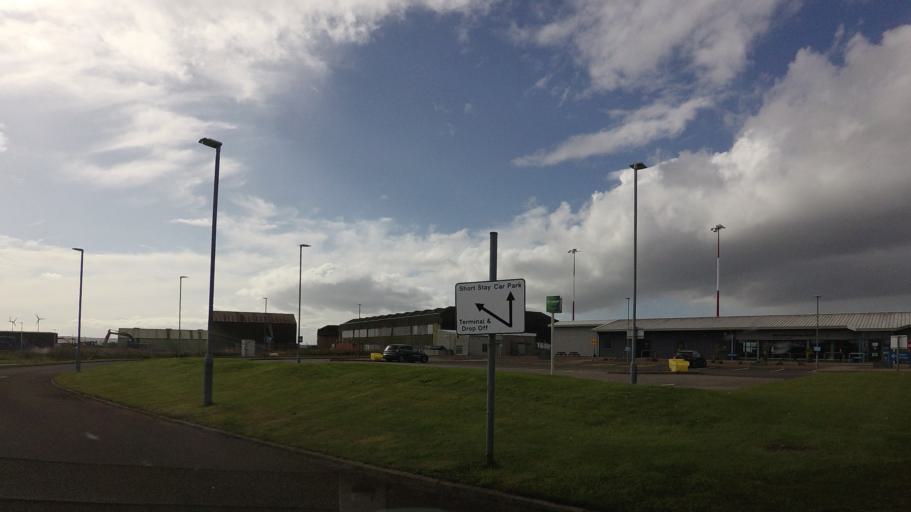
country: GB
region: Scotland
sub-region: Highland
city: Wick
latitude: 58.4531
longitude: -3.0866
